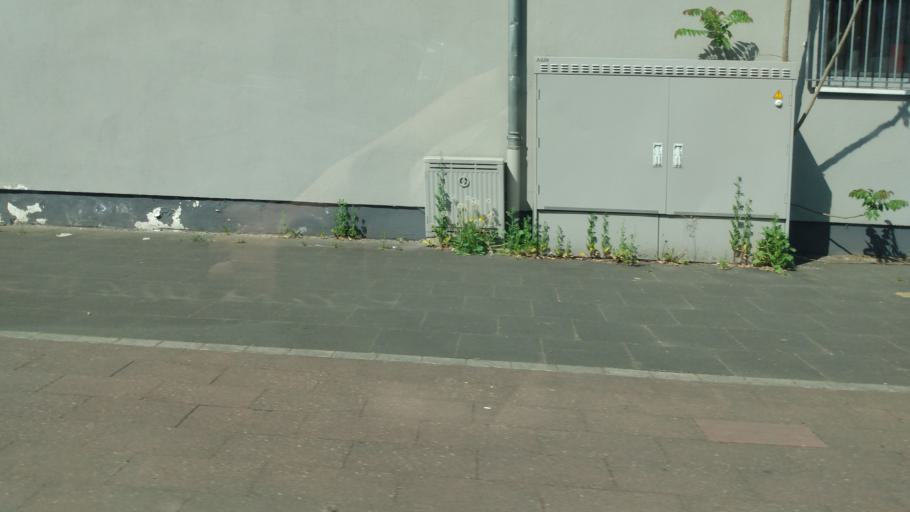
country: DE
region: North Rhine-Westphalia
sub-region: Regierungsbezirk Koln
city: Muelheim
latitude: 50.9964
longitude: 7.0367
